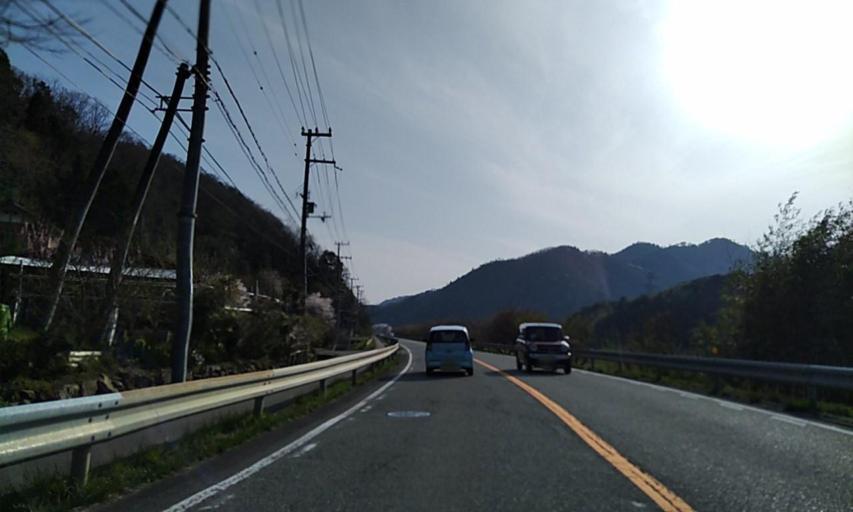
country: JP
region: Hyogo
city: Sasayama
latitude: 35.1125
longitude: 135.3264
